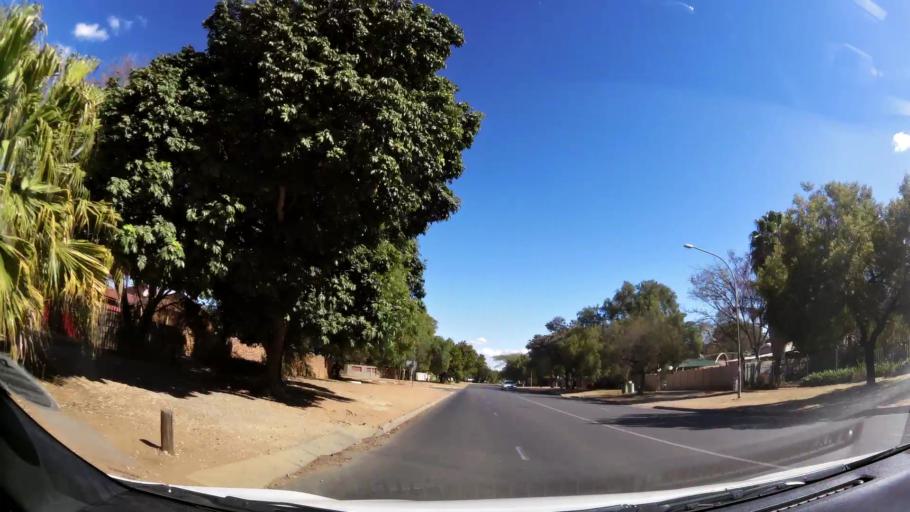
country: ZA
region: Limpopo
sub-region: Capricorn District Municipality
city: Polokwane
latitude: -23.9126
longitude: 29.4823
